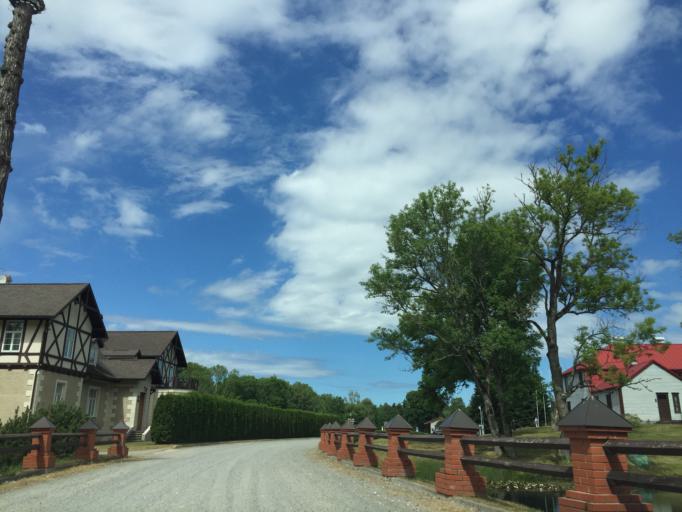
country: LV
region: Saulkrastu
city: Saulkrasti
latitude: 57.4040
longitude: 24.4251
